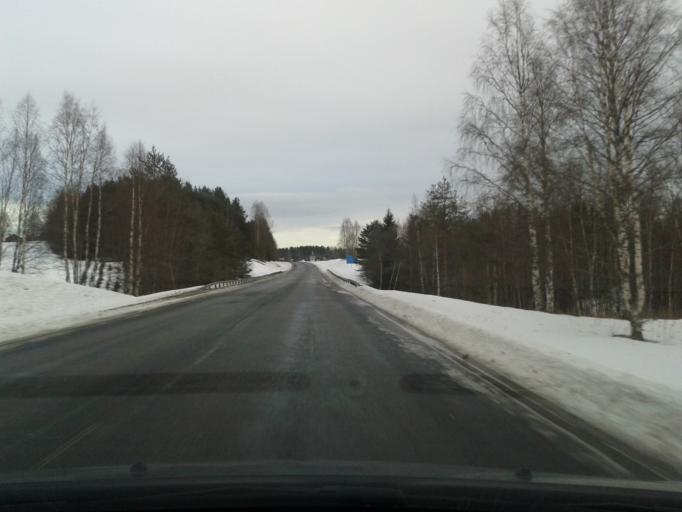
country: SE
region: Vaesternorrland
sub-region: Solleftea Kommun
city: As
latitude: 63.4536
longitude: 16.8977
